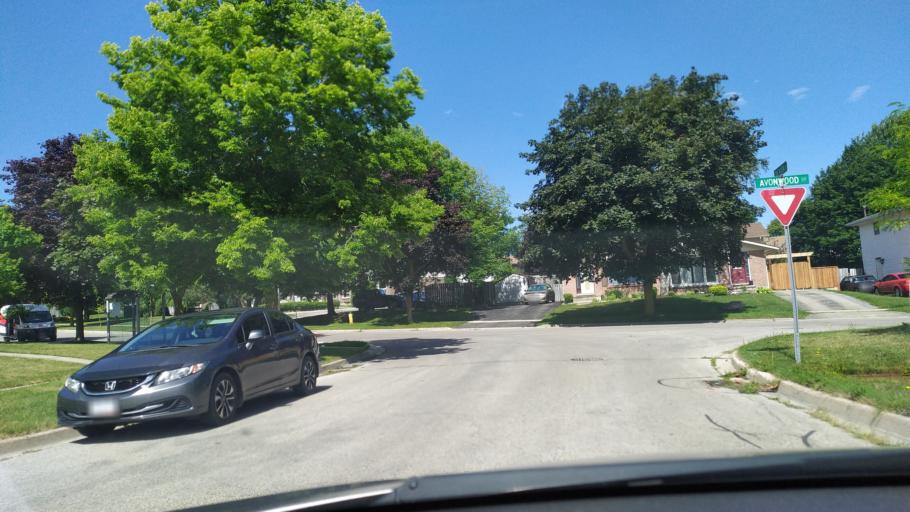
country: CA
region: Ontario
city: Stratford
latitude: 43.3728
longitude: -80.9462
